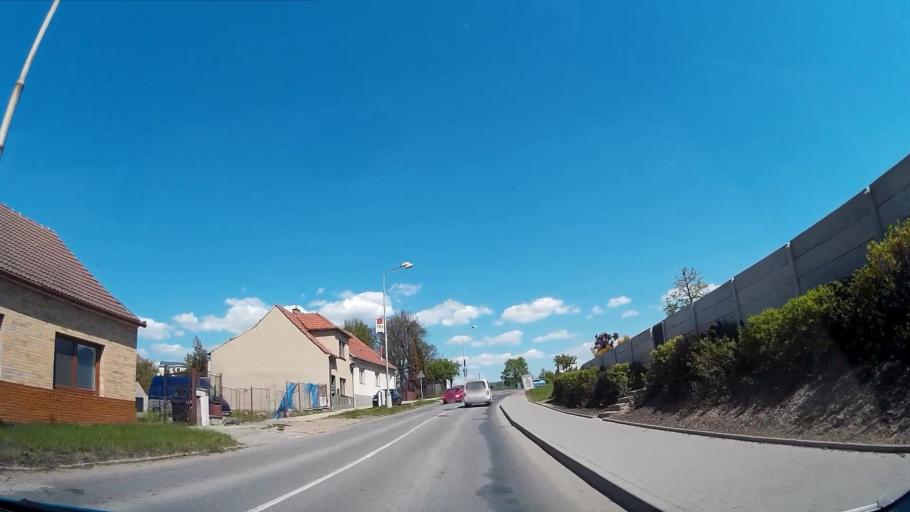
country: CZ
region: South Moravian
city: Ivancice
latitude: 49.1066
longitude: 16.3723
